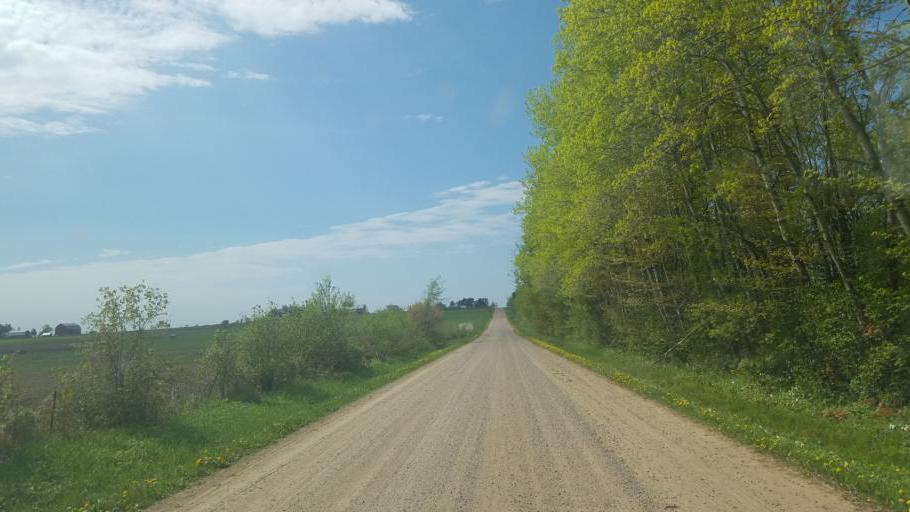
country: US
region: Wisconsin
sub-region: Marathon County
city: Spencer
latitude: 44.6046
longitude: -90.3765
